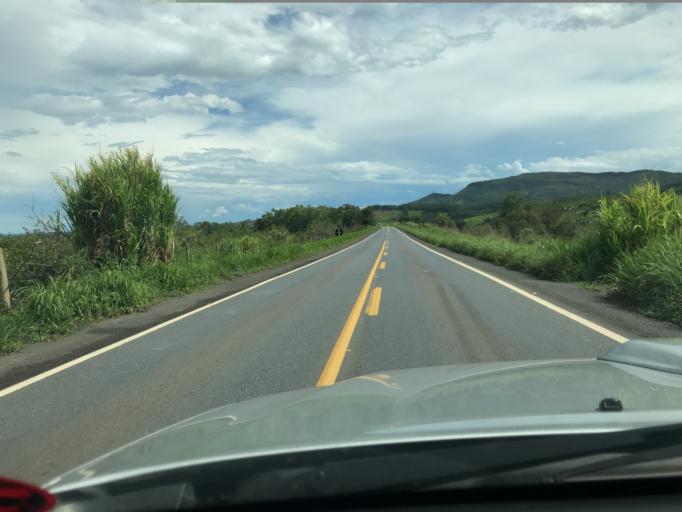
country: BR
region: Minas Gerais
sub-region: Campos Altos
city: Campos Altos
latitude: -19.7989
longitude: -46.0338
